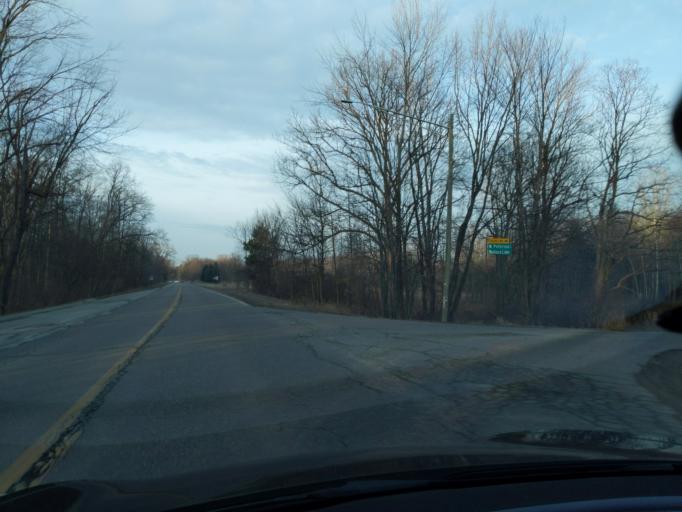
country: US
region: Michigan
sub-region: Livingston County
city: Brighton
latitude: 42.6064
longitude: -83.7483
